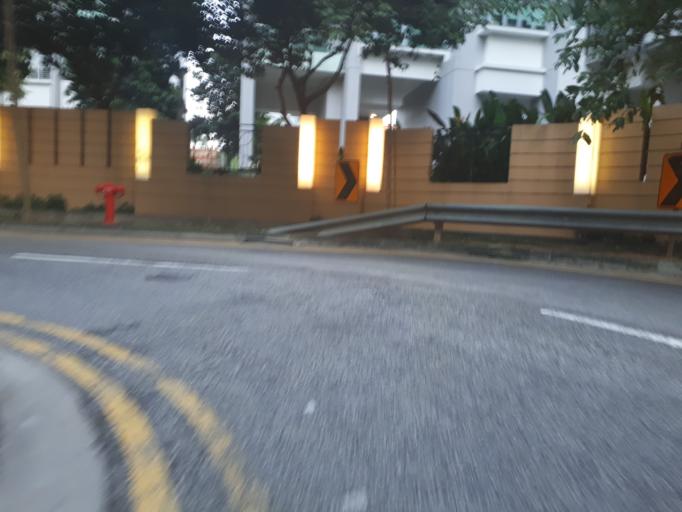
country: SG
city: Singapore
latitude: 1.3147
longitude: 103.8429
